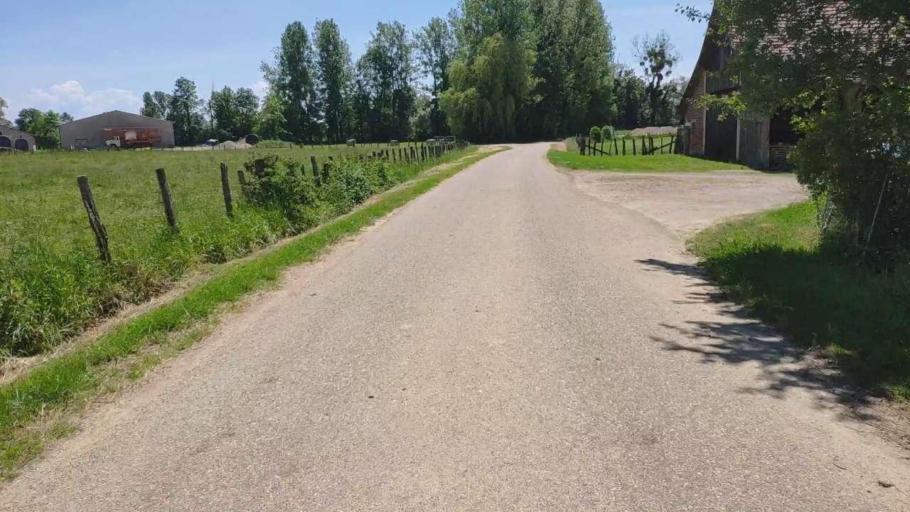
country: FR
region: Franche-Comte
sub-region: Departement du Jura
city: Bletterans
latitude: 46.7413
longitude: 5.4060
